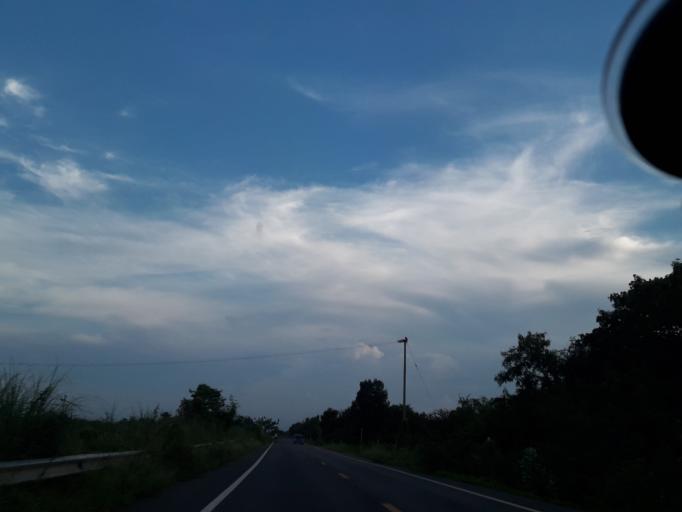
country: TH
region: Sara Buri
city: Nong Khae
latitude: 14.2935
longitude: 100.8911
